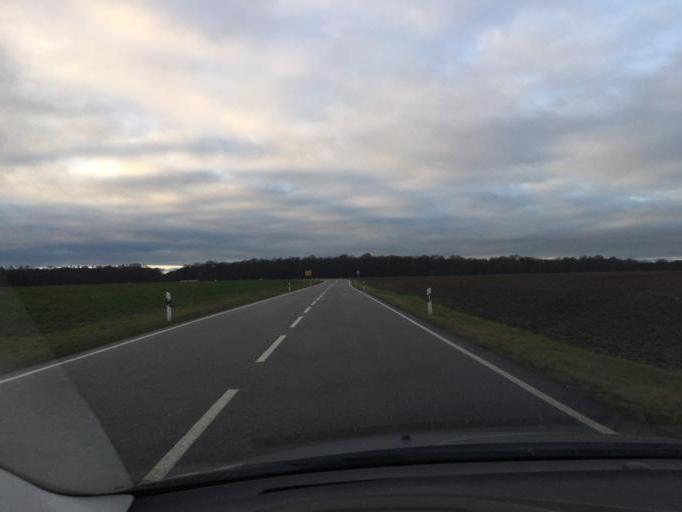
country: DE
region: Saxony
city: Frohburg
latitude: 51.0376
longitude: 12.5529
